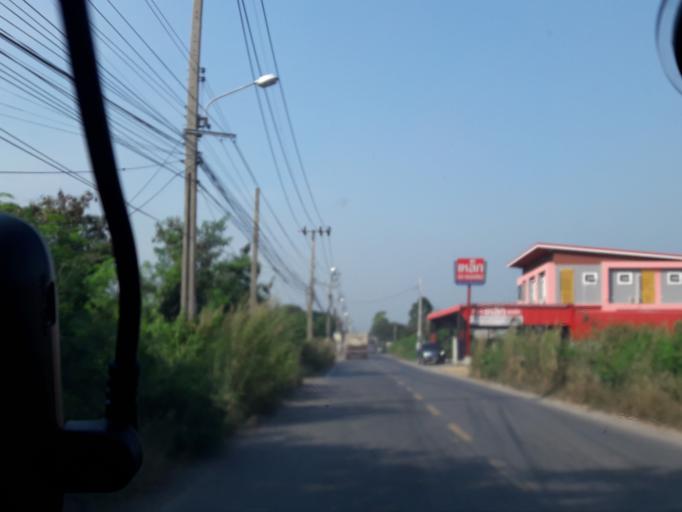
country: TH
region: Pathum Thani
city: Lam Luk Ka
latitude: 13.9106
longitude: 100.7363
